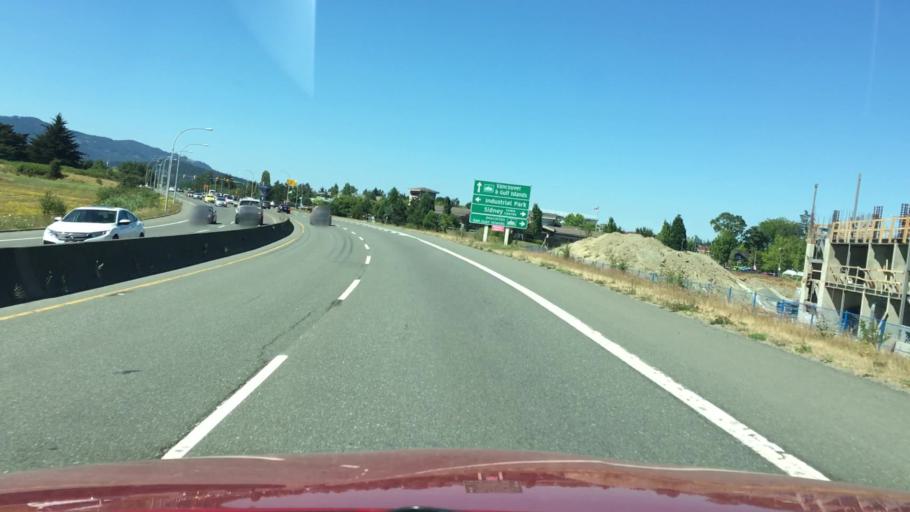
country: CA
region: British Columbia
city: North Saanich
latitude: 48.6460
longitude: -123.4052
